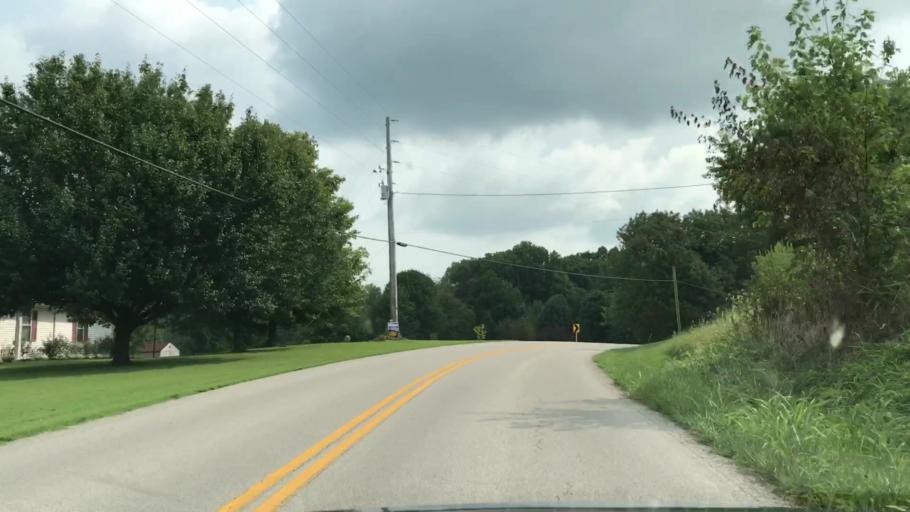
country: US
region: Kentucky
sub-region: Edmonson County
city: Brownsville
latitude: 37.1563
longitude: -86.2160
